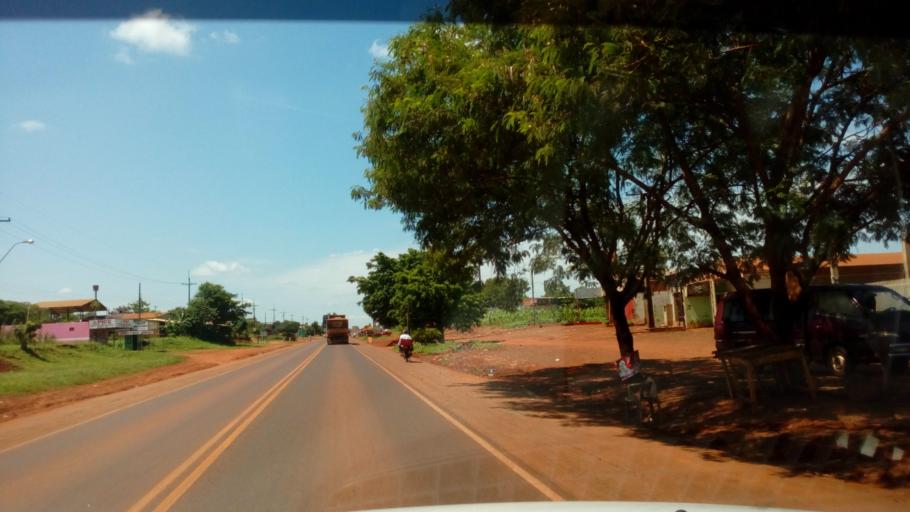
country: PY
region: Alto Parana
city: Colonia Yguazu
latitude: -25.4914
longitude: -54.8980
